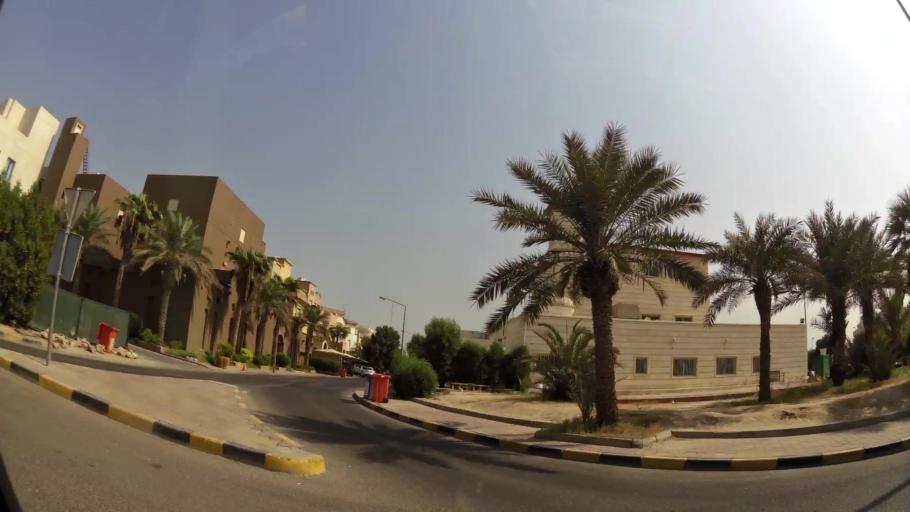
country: KW
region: Al Asimah
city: Ash Shamiyah
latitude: 29.3347
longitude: 47.9527
